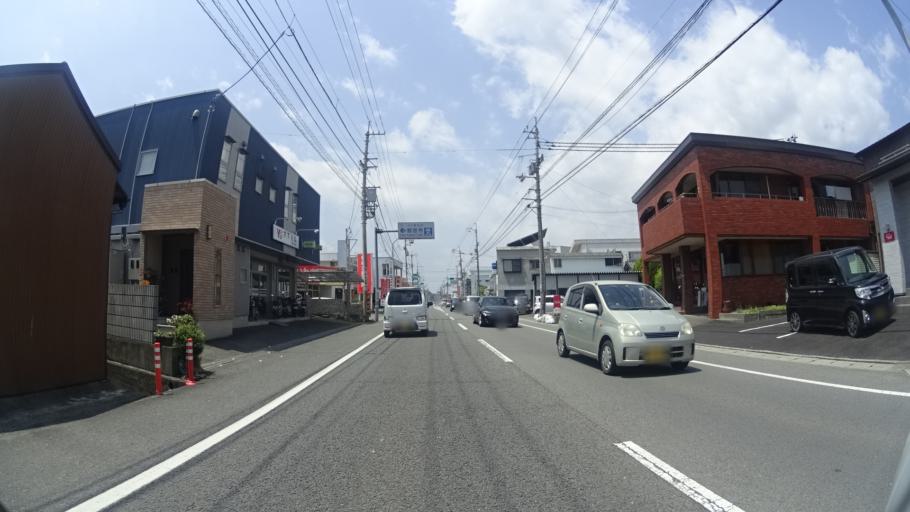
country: JP
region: Tokushima
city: Ishii
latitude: 34.0719
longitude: 134.4816
